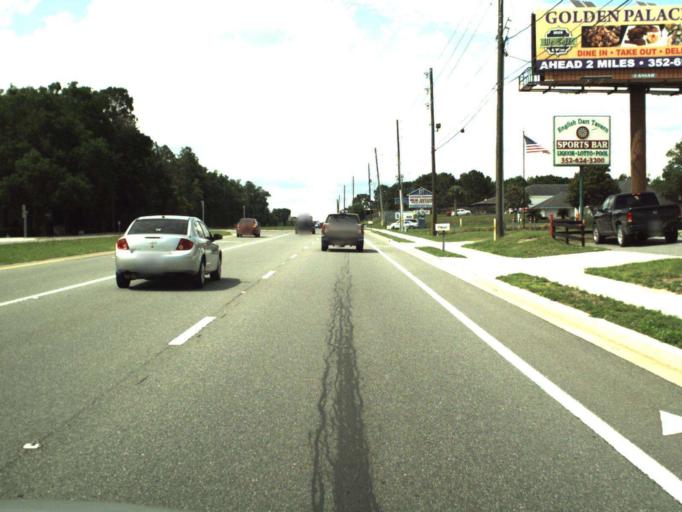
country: US
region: Florida
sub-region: Marion County
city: Silver Springs Shores
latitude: 29.1490
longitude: -82.0535
